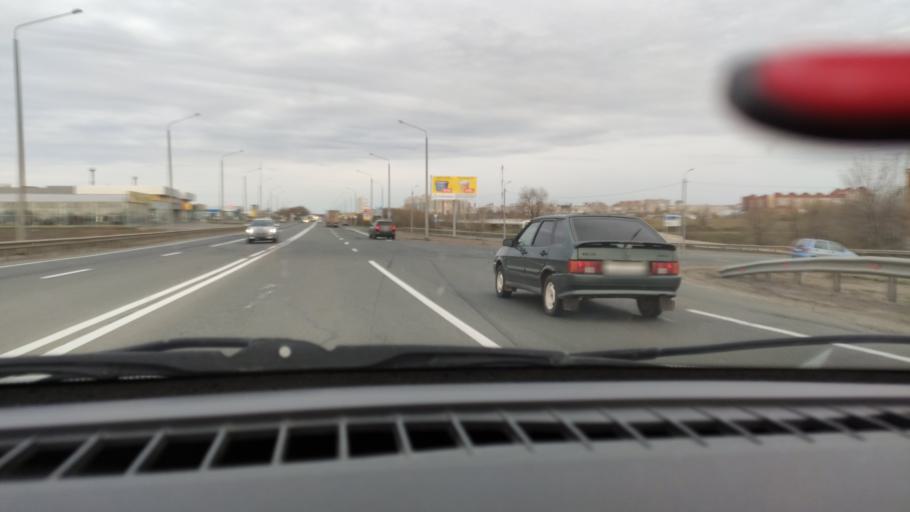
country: RU
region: Orenburg
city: Orenburg
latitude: 51.8490
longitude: 55.1455
